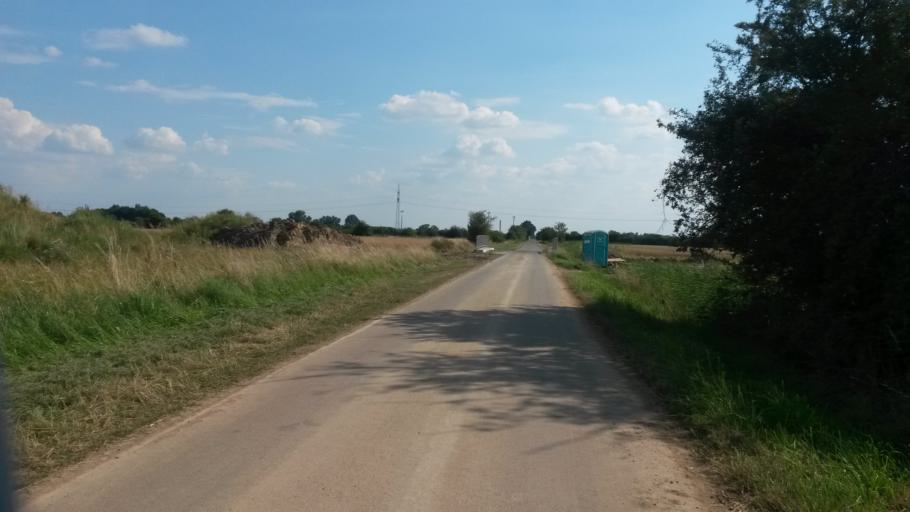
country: DE
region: Lower Saxony
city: Riede
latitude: 53.0235
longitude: 8.9106
